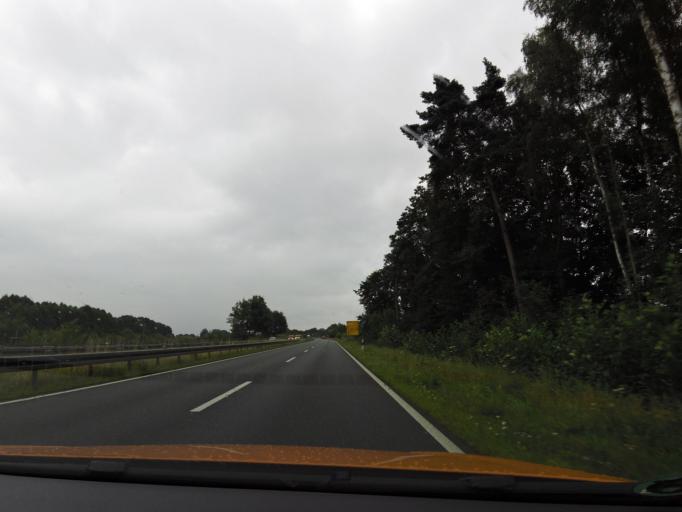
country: DE
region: Lower Saxony
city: Neustadt am Rubenberge
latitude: 52.5270
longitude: 9.4383
